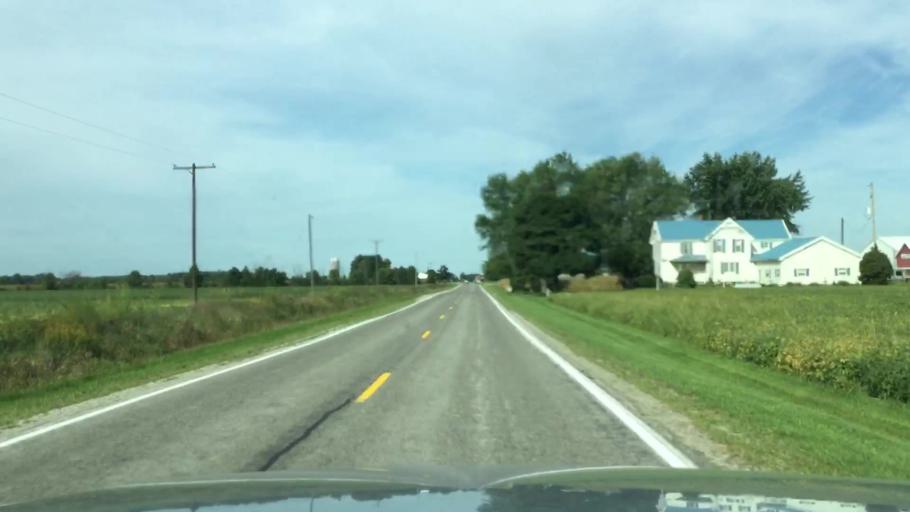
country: US
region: Michigan
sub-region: Genesee County
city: Montrose
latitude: 43.1469
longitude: -83.9744
